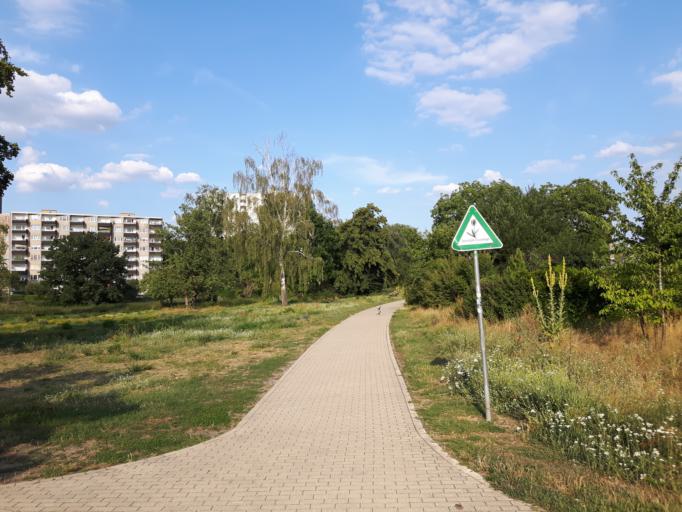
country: DE
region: Berlin
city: Falkenhagener Feld
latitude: 52.5427
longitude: 13.1760
